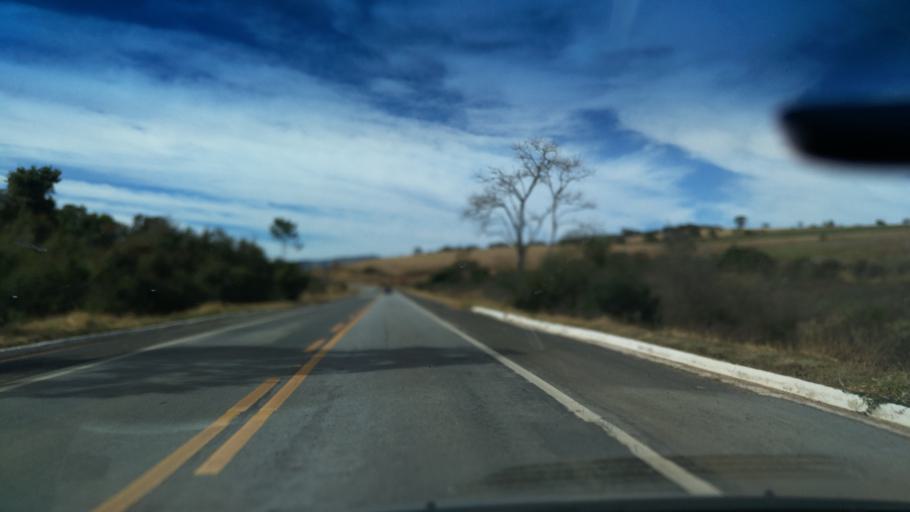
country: BR
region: Minas Gerais
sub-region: Borda Da Mata
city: Borda da Mata
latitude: -22.0624
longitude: -46.2787
